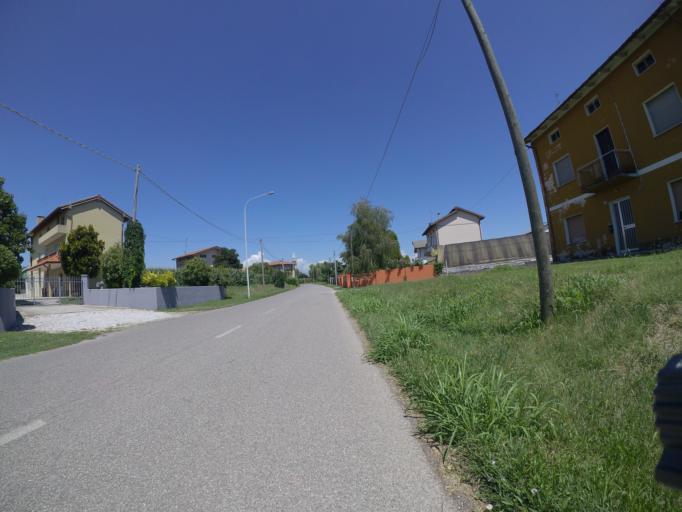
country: IT
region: Friuli Venezia Giulia
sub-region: Provincia di Udine
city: Talmassons
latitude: 45.9248
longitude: 13.1141
